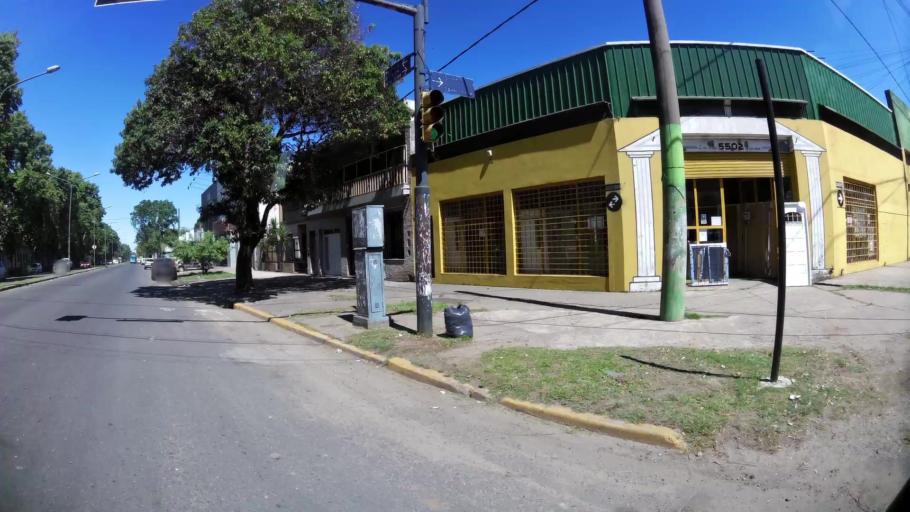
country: AR
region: Santa Fe
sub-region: Departamento de Rosario
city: Rosario
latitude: -32.9610
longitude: -60.6977
